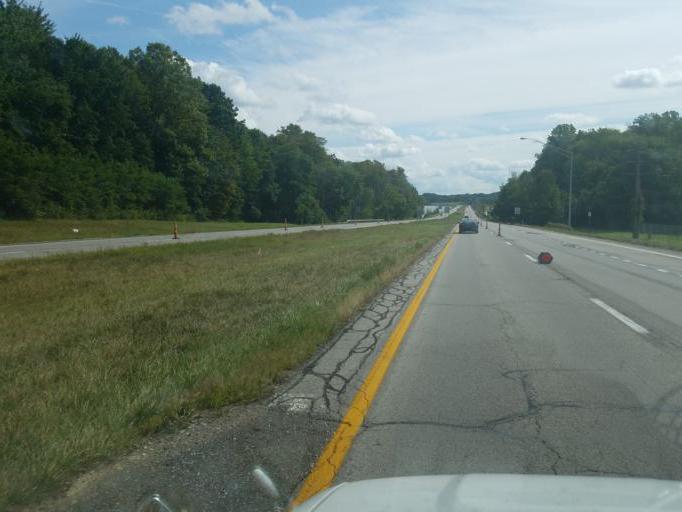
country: US
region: Ohio
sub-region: Portage County
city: Hiram
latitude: 41.3837
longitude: -81.2111
